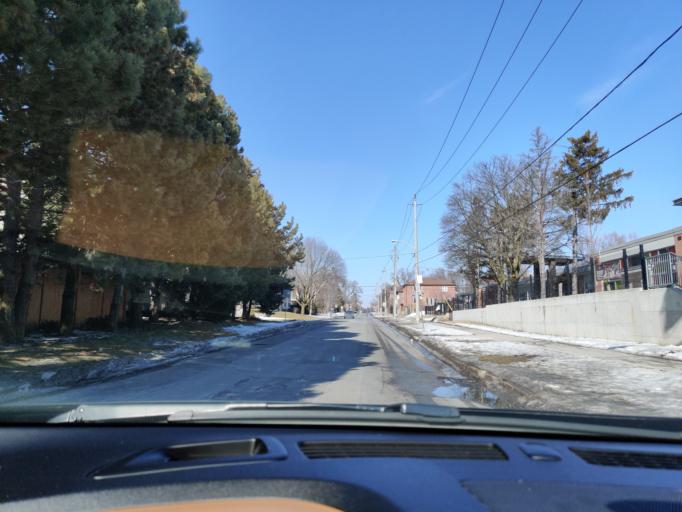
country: CA
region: Ontario
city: Toronto
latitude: 43.7158
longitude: -79.4318
